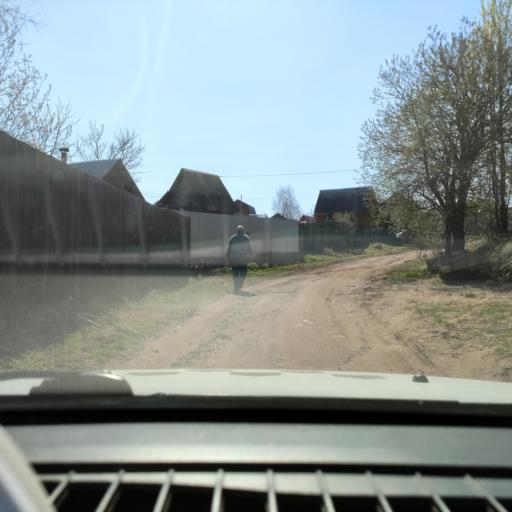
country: RU
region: Perm
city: Perm
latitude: 58.0684
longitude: 56.3758
